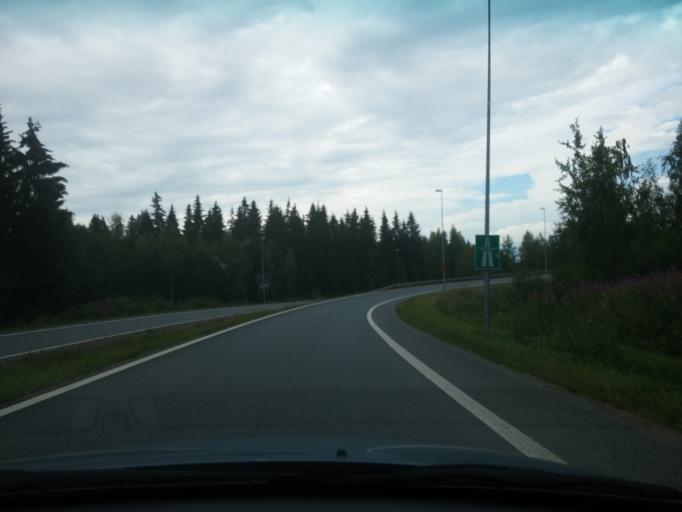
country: FI
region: Haeme
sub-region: Riihimaeki
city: Riihimaeki
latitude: 60.7507
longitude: 24.7273
